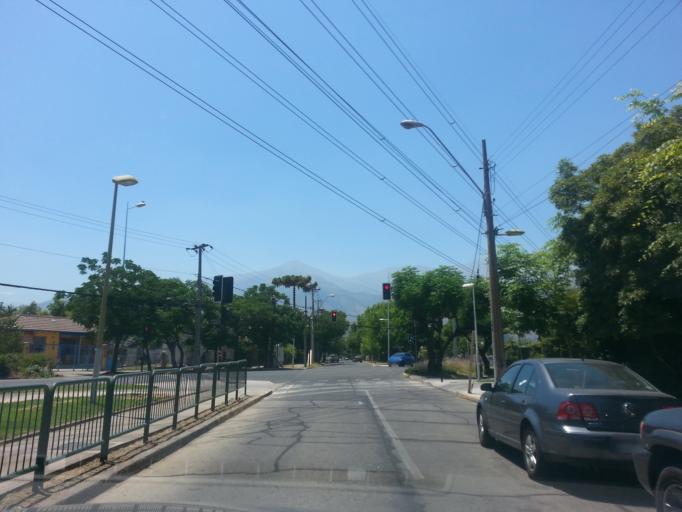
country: CL
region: Santiago Metropolitan
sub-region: Provincia de Santiago
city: Villa Presidente Frei, Nunoa, Santiago, Chile
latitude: -33.4142
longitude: -70.5584
